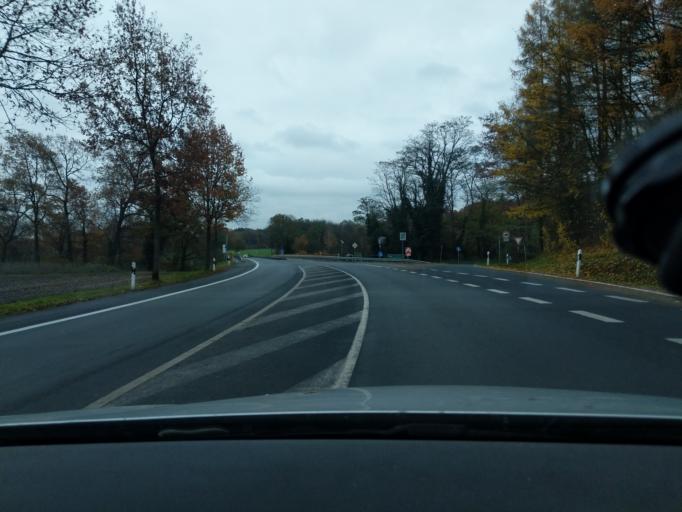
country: DE
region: North Rhine-Westphalia
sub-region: Regierungsbezirk Munster
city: Horstel
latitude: 52.2808
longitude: 7.6031
